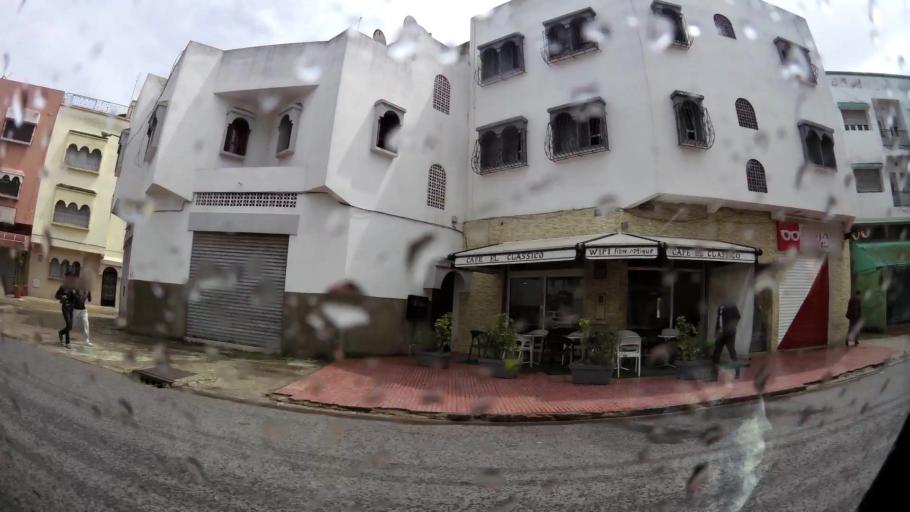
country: MA
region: Grand Casablanca
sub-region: Casablanca
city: Casablanca
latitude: 33.5497
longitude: -7.6840
